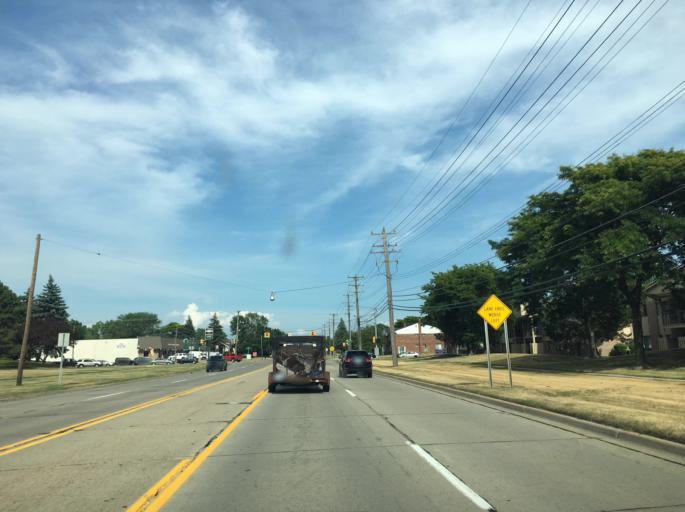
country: US
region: Michigan
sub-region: Macomb County
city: Fraser
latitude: 42.5393
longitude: -82.9312
